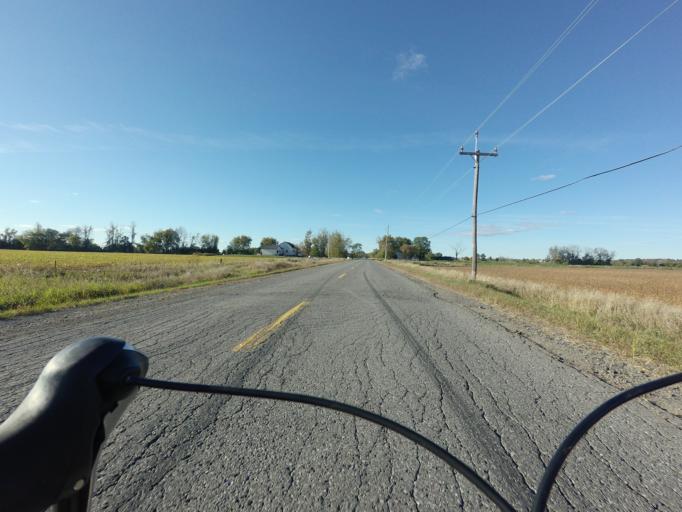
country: CA
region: Ontario
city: Bells Corners
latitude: 45.2164
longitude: -75.7996
